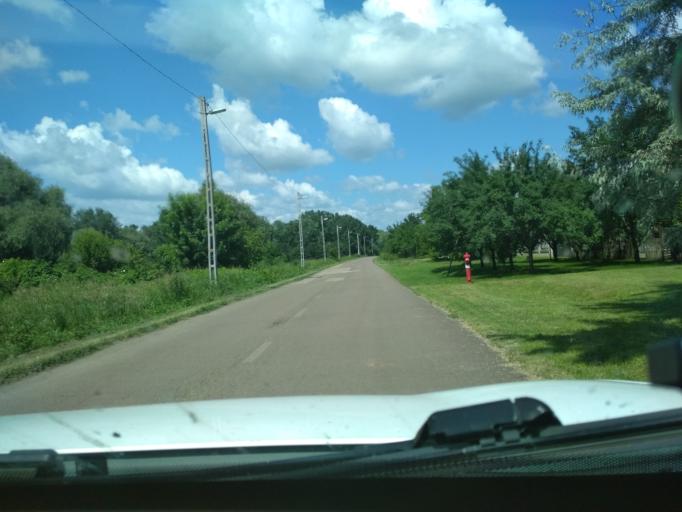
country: HU
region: Jasz-Nagykun-Szolnok
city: Abadszalok
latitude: 47.4830
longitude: 20.5951
